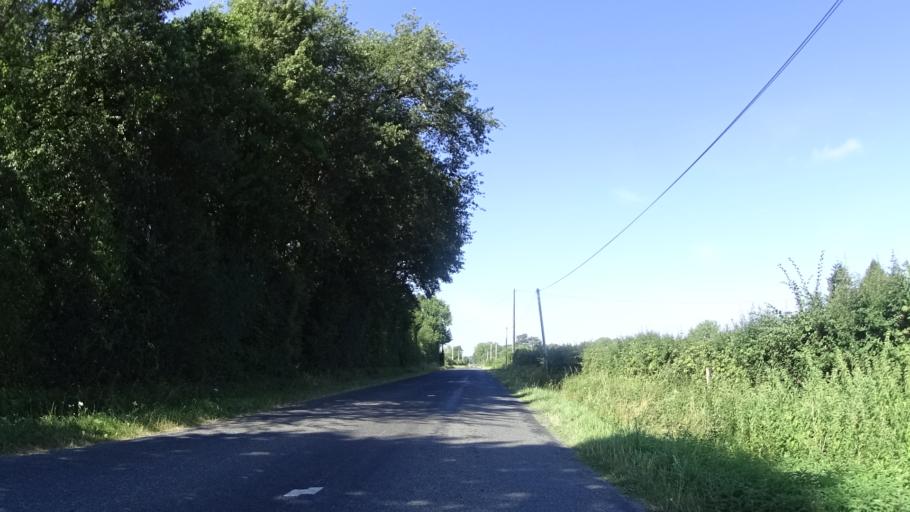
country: FR
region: Pays de la Loire
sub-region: Departement de Maine-et-Loire
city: Etriche
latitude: 47.6320
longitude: -0.4381
